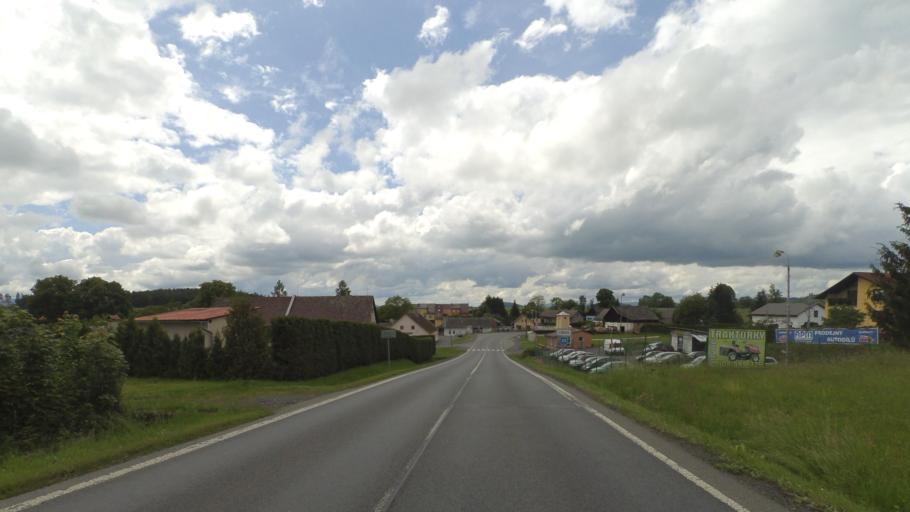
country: CZ
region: Plzensky
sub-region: Okres Klatovy
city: Nyrsko
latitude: 49.3671
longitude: 13.1358
